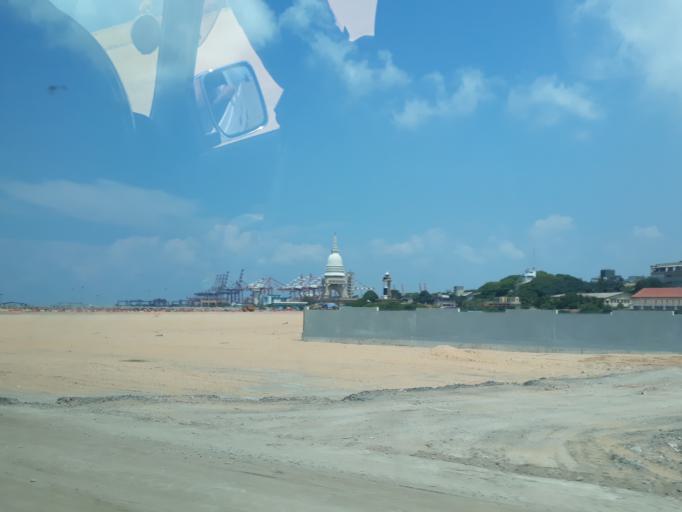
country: LK
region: Western
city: Colombo
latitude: 6.9334
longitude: 79.8385
